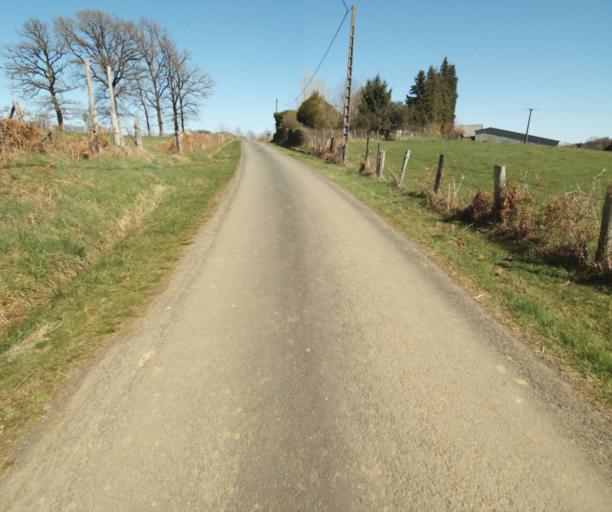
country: FR
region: Limousin
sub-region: Departement de la Correze
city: Seilhac
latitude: 45.3843
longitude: 1.6815
